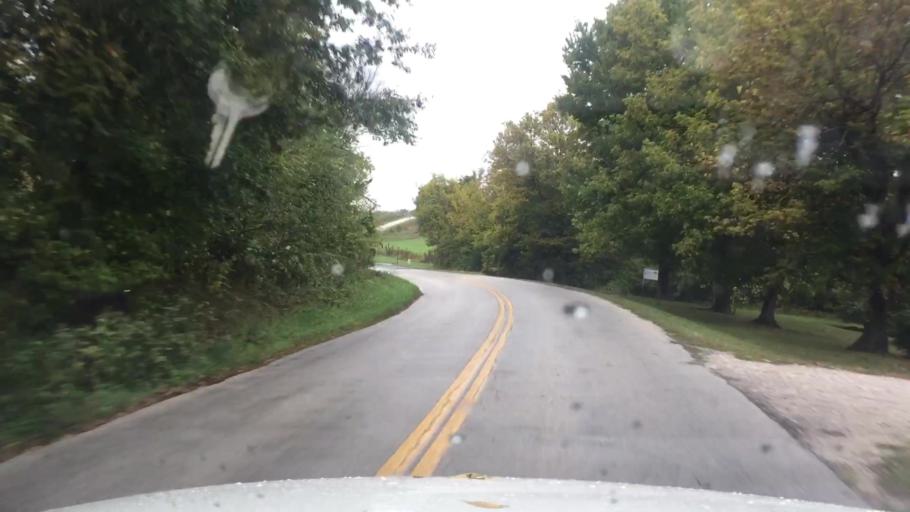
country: US
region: Missouri
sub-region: Boone County
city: Columbia
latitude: 38.9222
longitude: -92.4674
